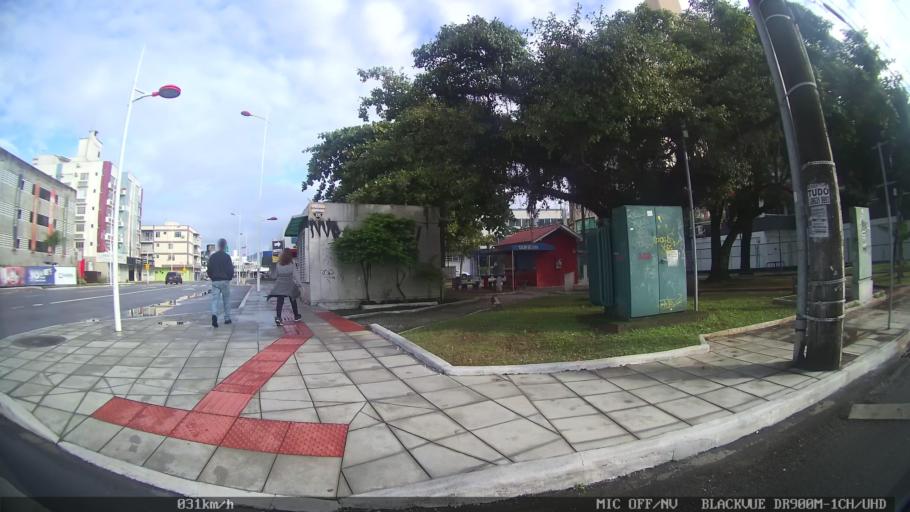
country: BR
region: Santa Catarina
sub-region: Sao Jose
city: Campinas
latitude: -27.6017
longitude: -48.6166
